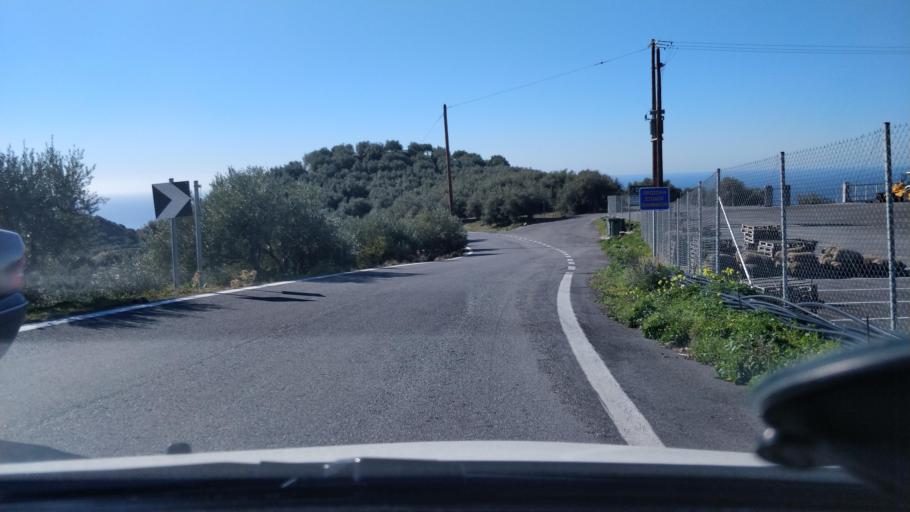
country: GR
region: Crete
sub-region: Nomos Irakleiou
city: Arkalochori
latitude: 35.0092
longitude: 25.4426
